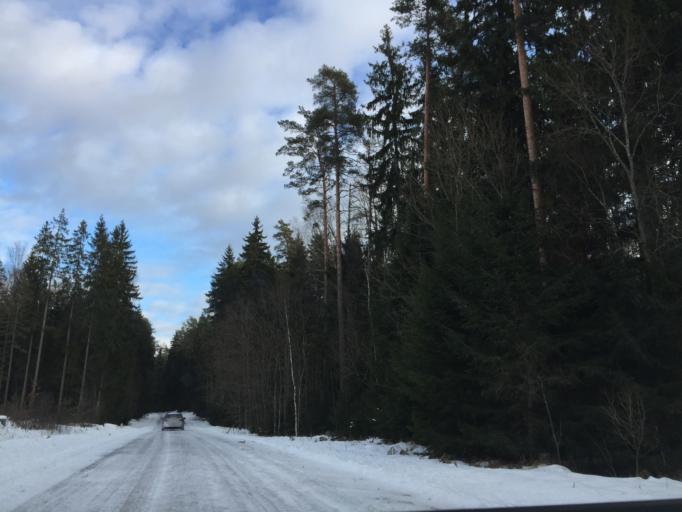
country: LV
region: Lielvarde
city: Lielvarde
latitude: 56.5621
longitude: 24.8010
